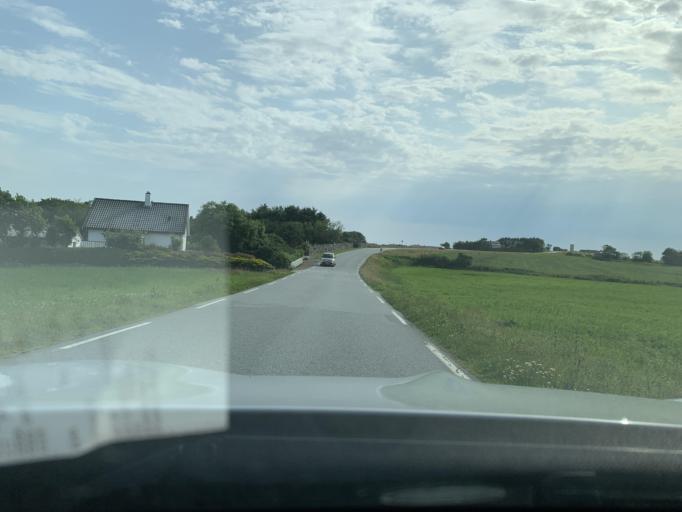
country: NO
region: Rogaland
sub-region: Time
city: Bryne
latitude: 58.7261
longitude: 5.5842
